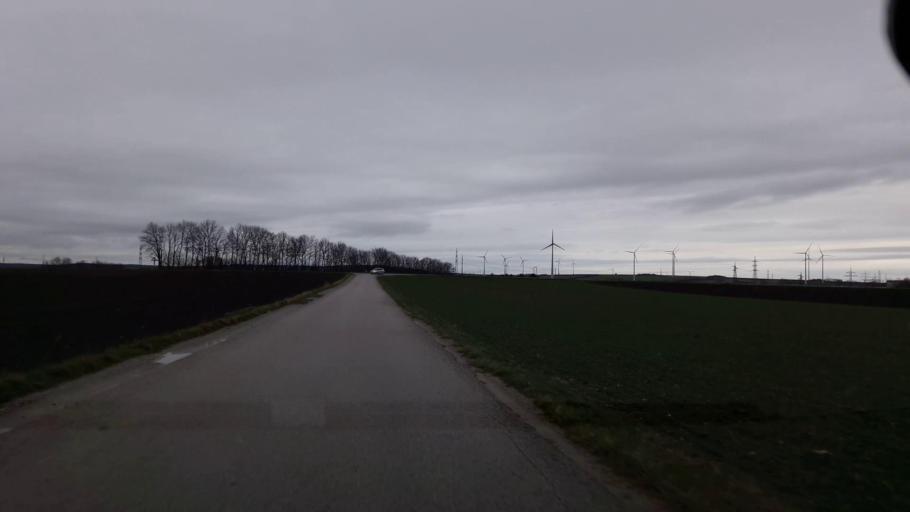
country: AT
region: Lower Austria
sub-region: Politischer Bezirk Bruck an der Leitha
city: Bruck an der Leitha
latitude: 48.0258
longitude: 16.7603
